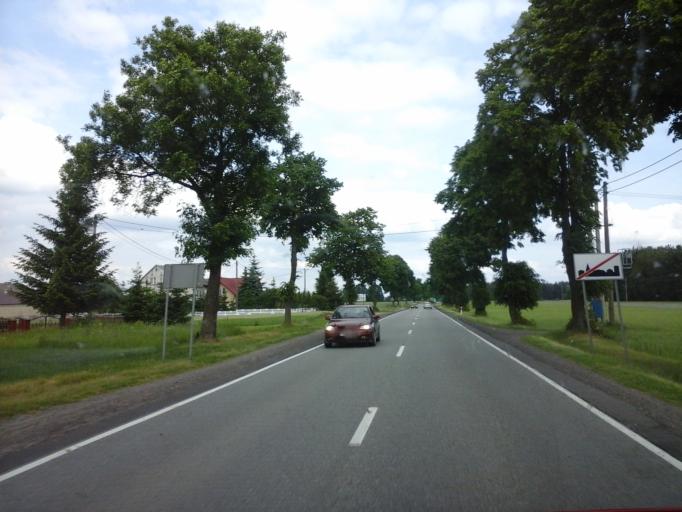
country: PL
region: Lodz Voivodeship
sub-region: Powiat opoczynski
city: Paradyz
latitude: 51.3137
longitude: 20.0747
